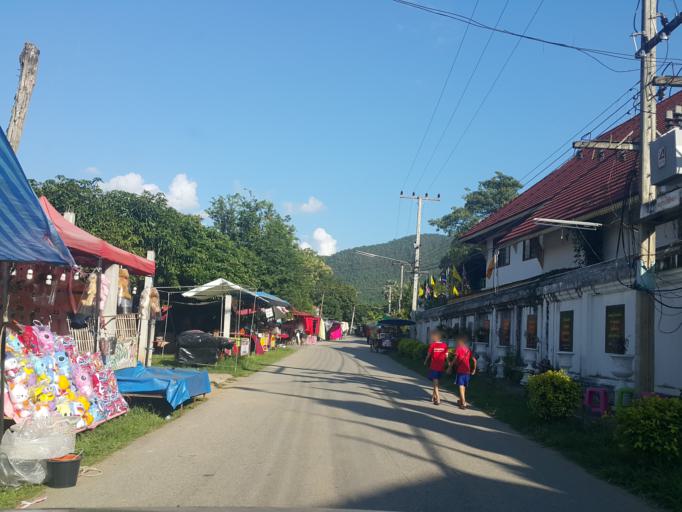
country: TH
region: Chiang Mai
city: Mae On
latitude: 18.7207
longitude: 99.2091
